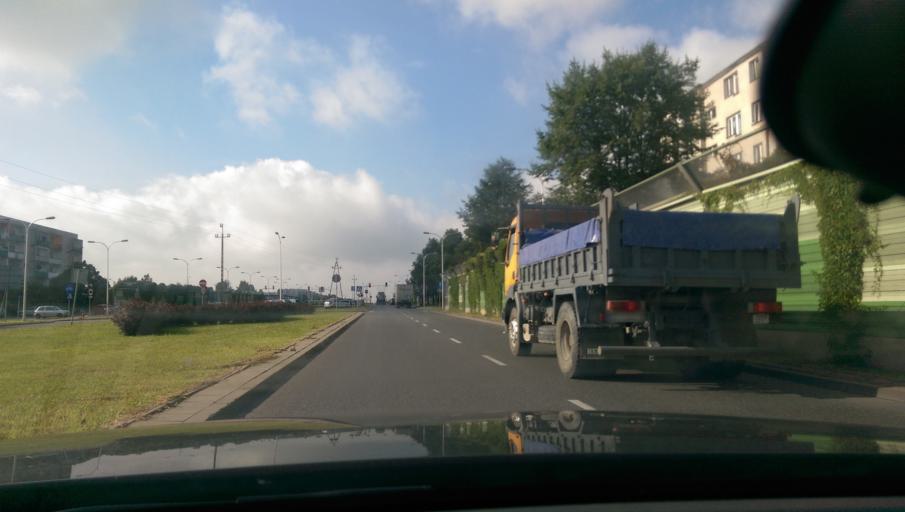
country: PL
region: Masovian Voivodeship
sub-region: Powiat ciechanowski
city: Ciechanow
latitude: 52.8810
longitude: 20.6281
